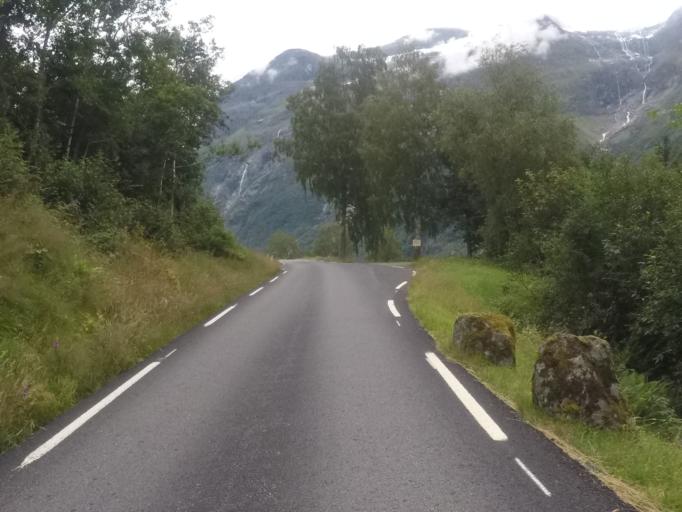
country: NO
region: Sogn og Fjordane
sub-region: Stryn
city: Stryn
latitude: 61.8350
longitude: 6.9490
